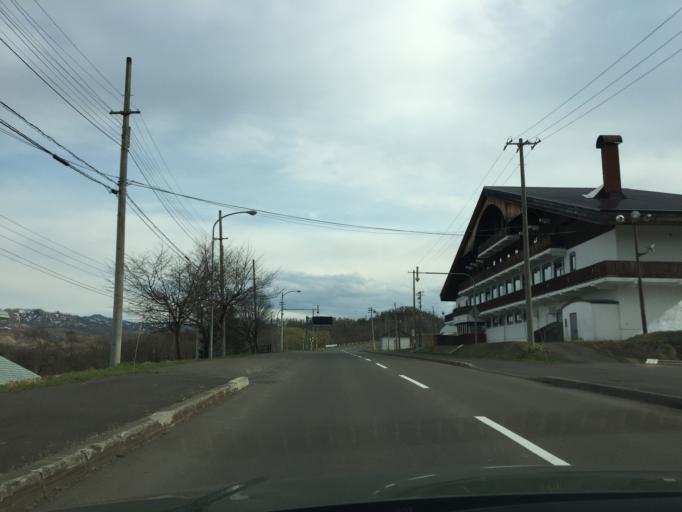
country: JP
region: Hokkaido
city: Utashinai
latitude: 43.5212
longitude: 142.0194
